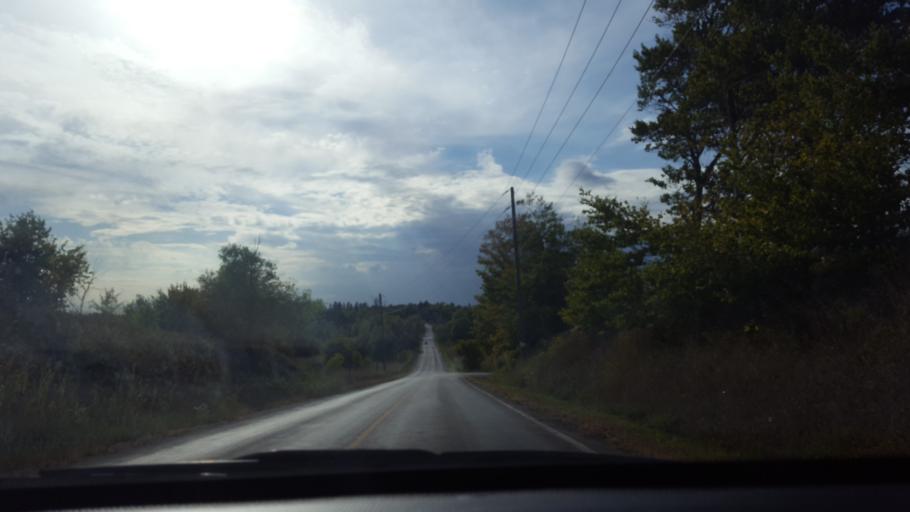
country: CA
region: Ontario
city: Vaughan
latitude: 43.8928
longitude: -79.6076
